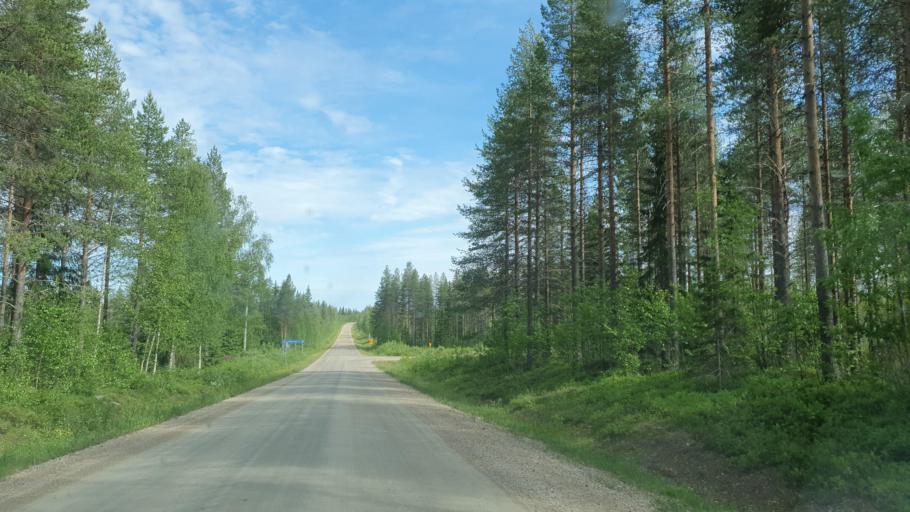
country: FI
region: Kainuu
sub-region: Kehys-Kainuu
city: Kuhmo
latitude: 64.4901
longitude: 29.5019
